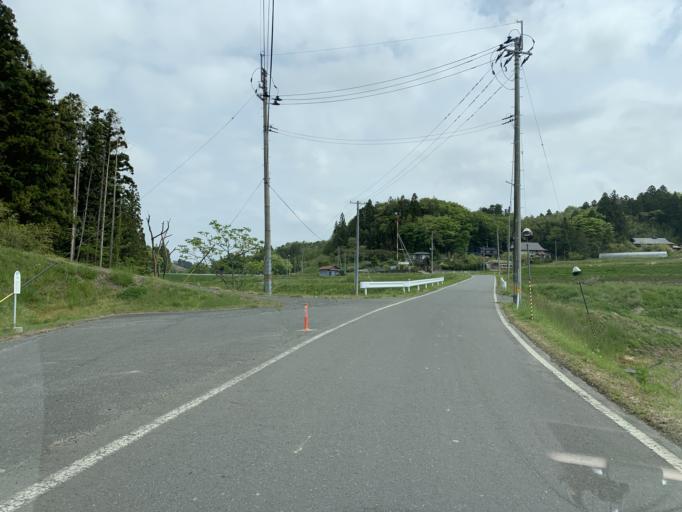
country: JP
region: Iwate
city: Ichinoseki
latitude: 38.8501
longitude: 141.1964
